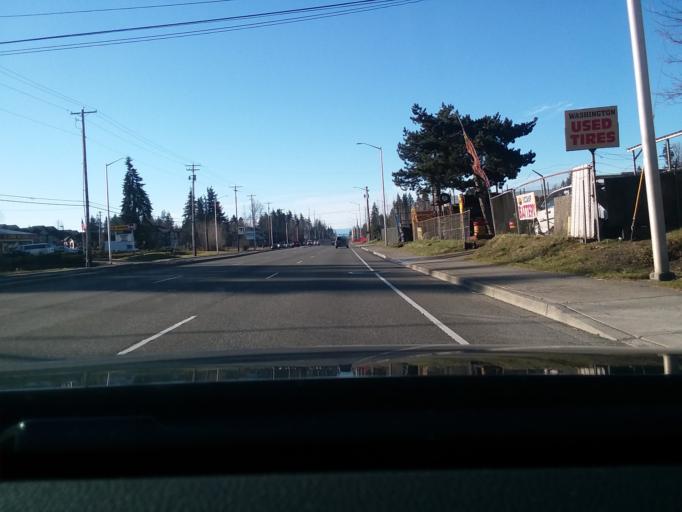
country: US
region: Washington
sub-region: Pierce County
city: Summit
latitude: 47.1295
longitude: -122.3575
